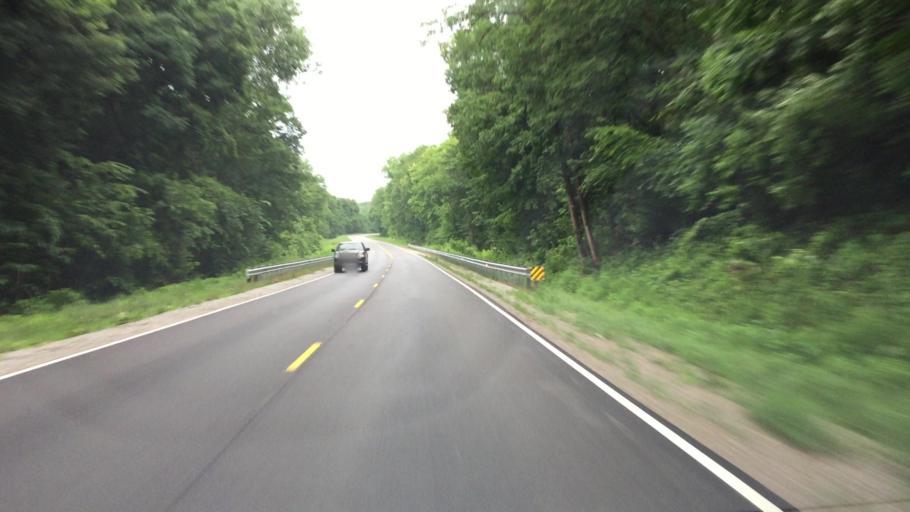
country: US
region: Iowa
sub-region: Lee County
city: Keokuk
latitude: 40.3722
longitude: -91.3952
